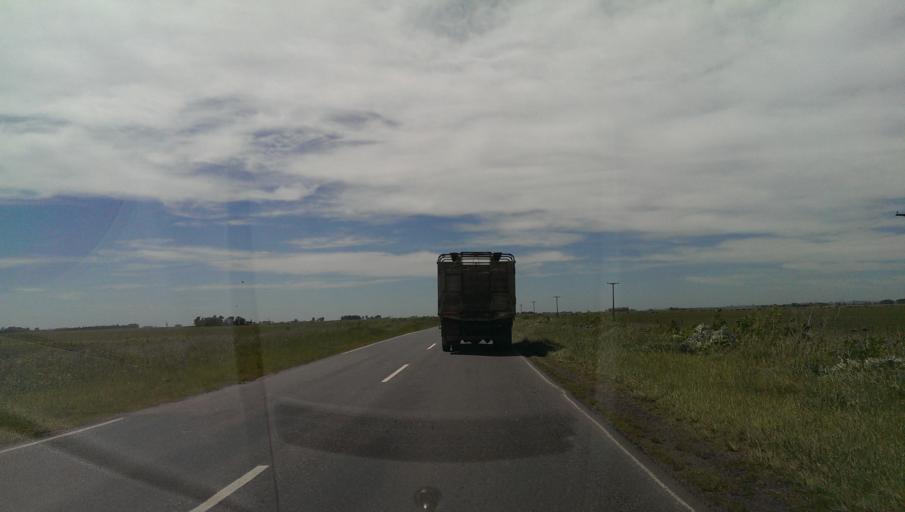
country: AR
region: Buenos Aires
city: Olavarria
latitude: -37.0682
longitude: -60.4680
